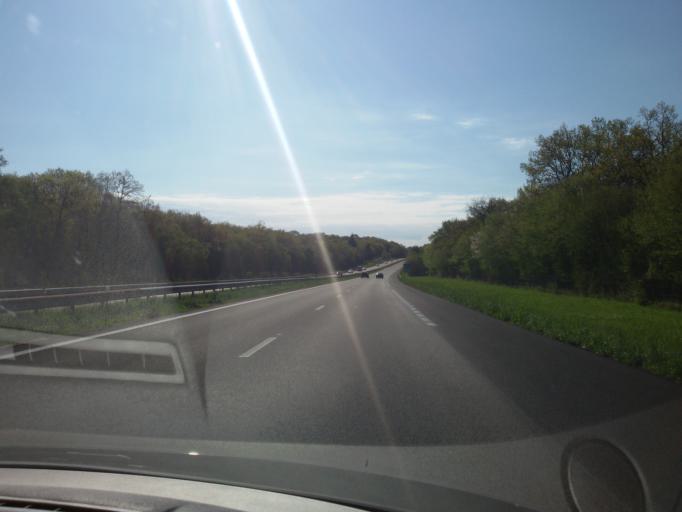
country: FR
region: Bourgogne
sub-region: Departement de l'Yonne
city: Joux-la-Ville
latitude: 47.6910
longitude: 3.8406
